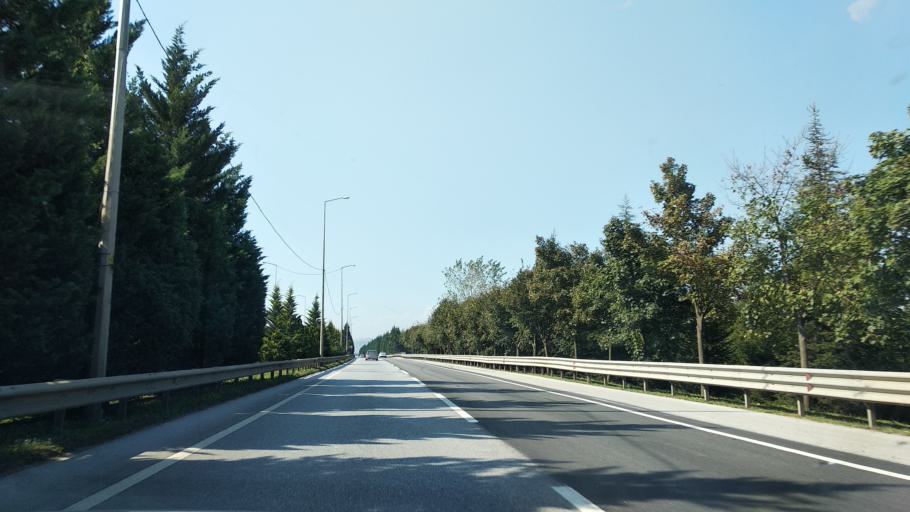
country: TR
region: Kocaeli
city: Kosekoy
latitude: 40.7553
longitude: 30.0108
